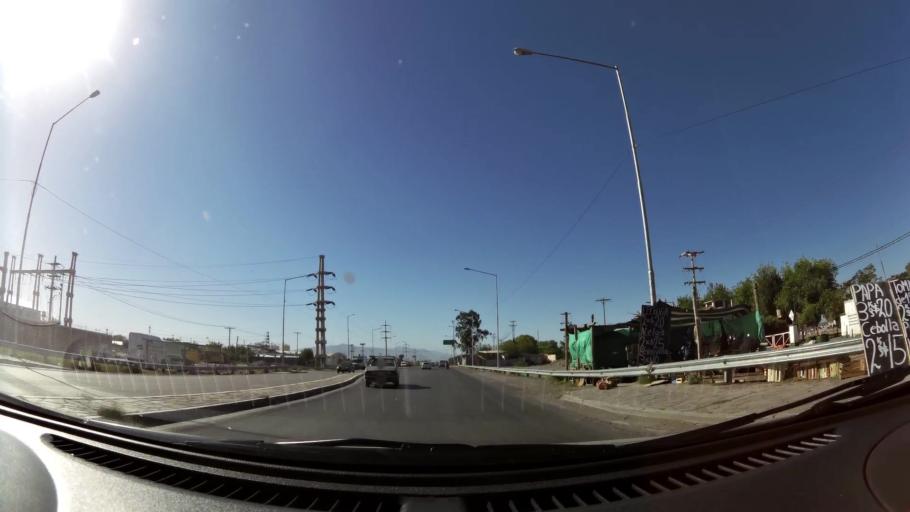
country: AR
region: San Juan
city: Villa Paula de Sarmiento
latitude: -31.5095
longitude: -68.5175
